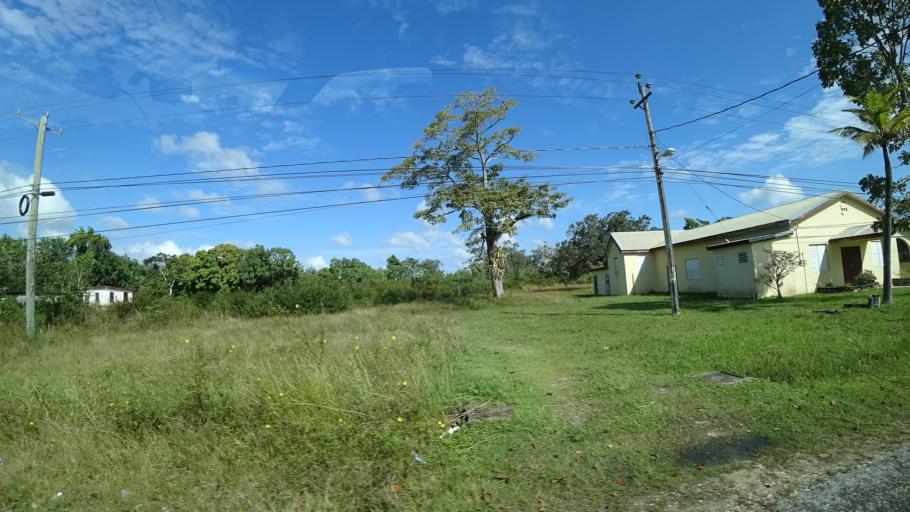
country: BZ
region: Belize
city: Belize City
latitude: 17.5692
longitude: -88.4017
